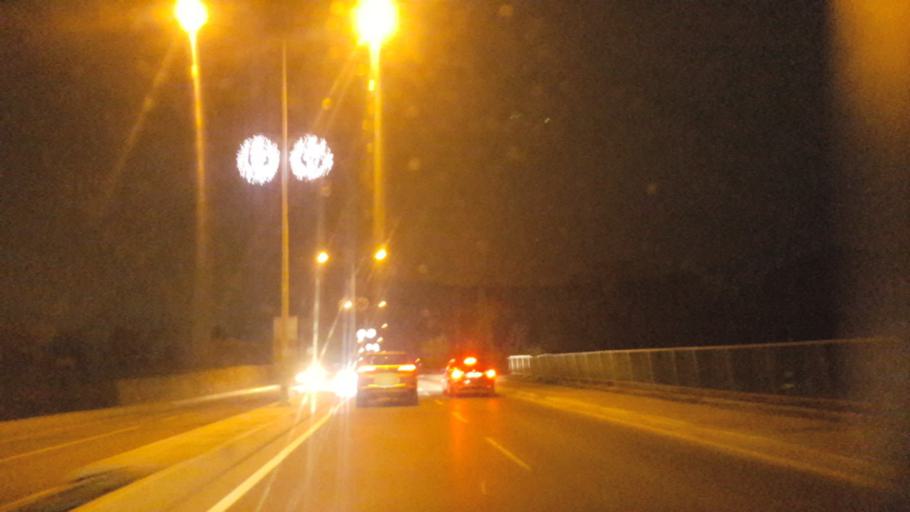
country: TR
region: Istanbul
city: Icmeler
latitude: 40.8316
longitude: 29.3262
